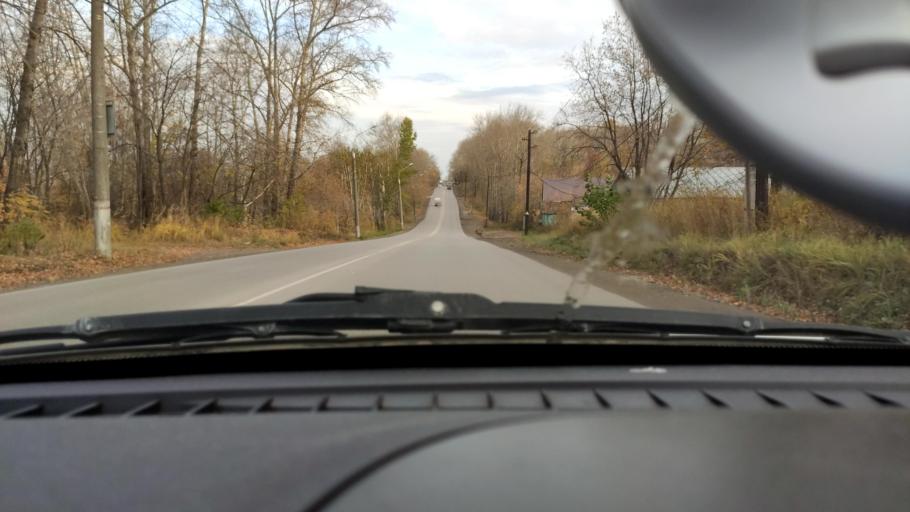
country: RU
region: Perm
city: Perm
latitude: 58.1229
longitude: 56.3700
